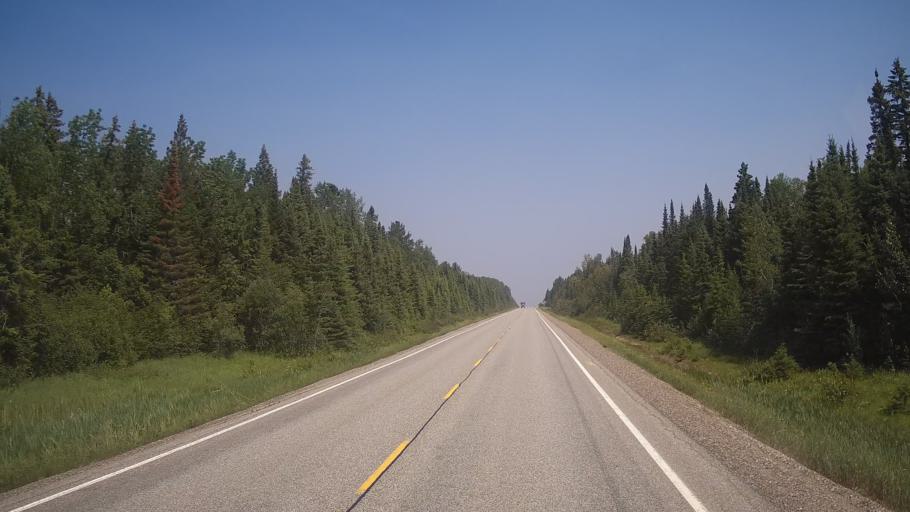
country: CA
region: Ontario
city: Timmins
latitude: 48.1973
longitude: -81.5811
